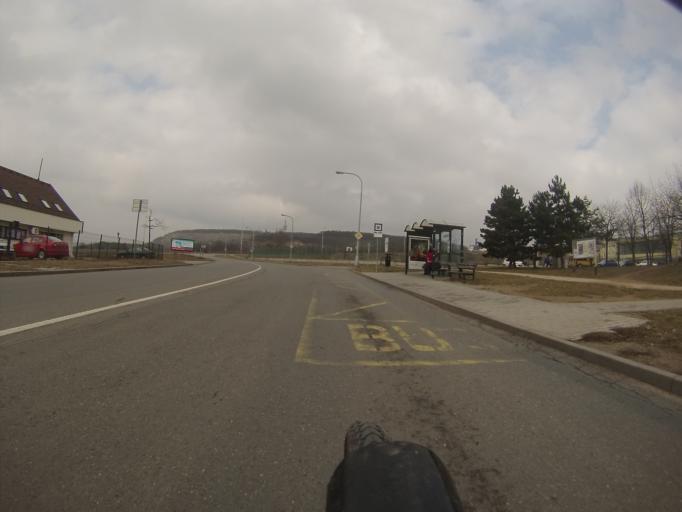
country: CZ
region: South Moravian
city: Bilovice nad Svitavou
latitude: 49.2119
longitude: 16.6766
